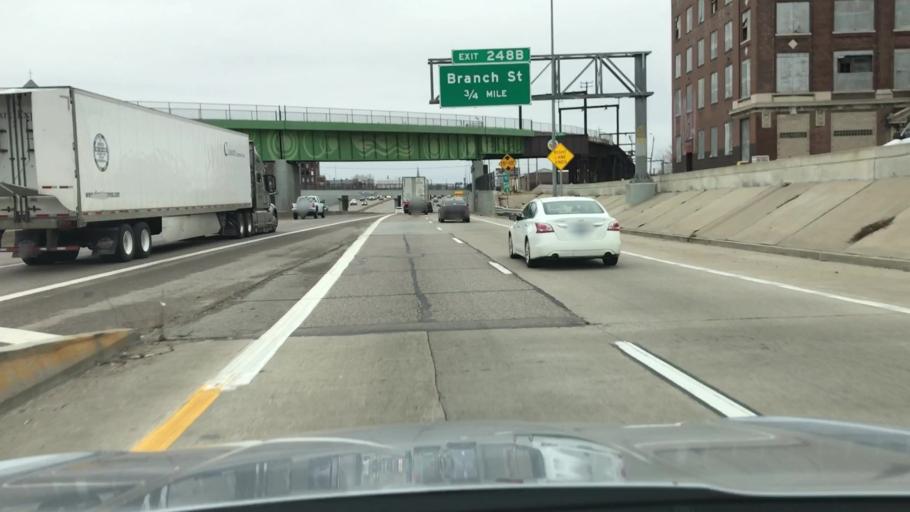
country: US
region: Missouri
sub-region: City of Saint Louis
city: St. Louis
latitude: 38.6452
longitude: -90.1898
